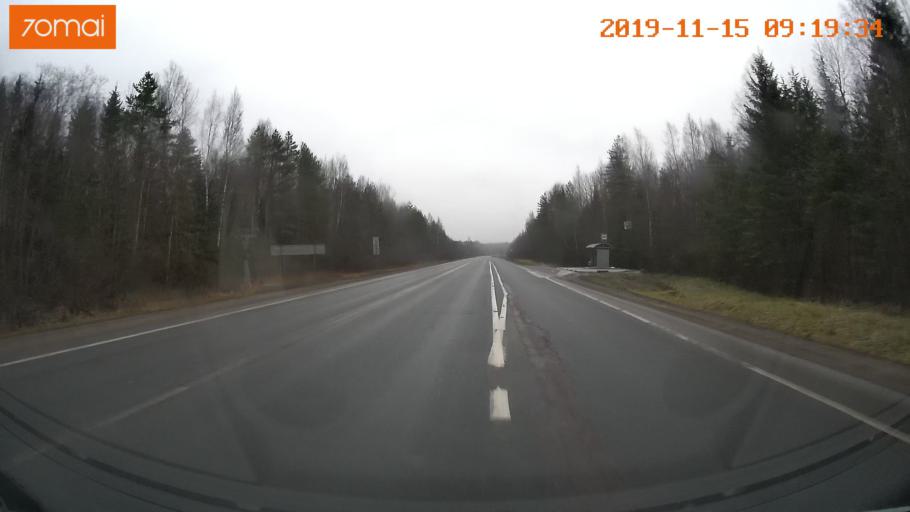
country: RU
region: Vologda
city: Tonshalovo
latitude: 59.2848
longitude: 38.0186
